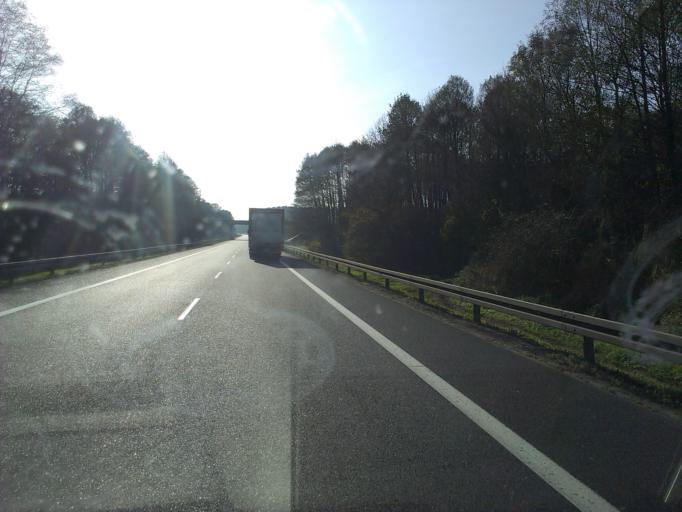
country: PL
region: Lubusz
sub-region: Zielona Gora
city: Zielona Gora
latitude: 51.9904
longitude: 15.5719
